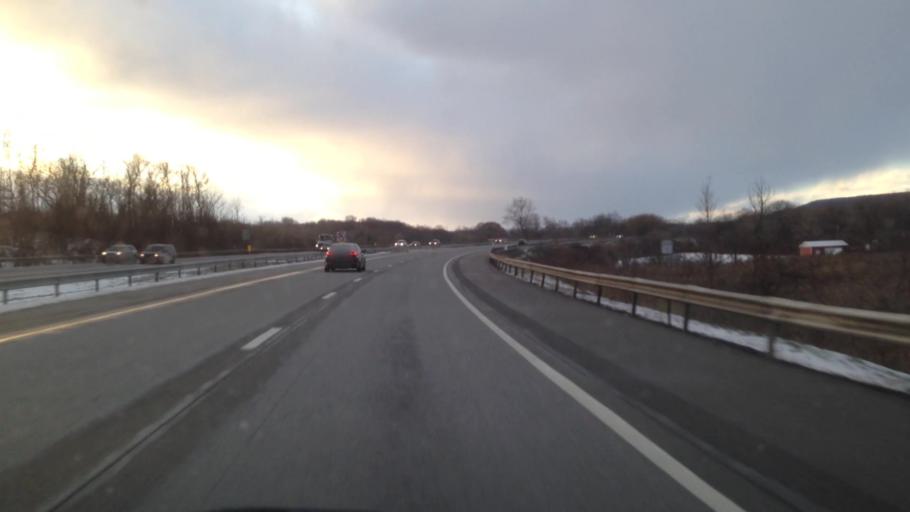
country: US
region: New York
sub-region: Herkimer County
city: Herkimer
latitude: 43.0139
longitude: -74.9709
